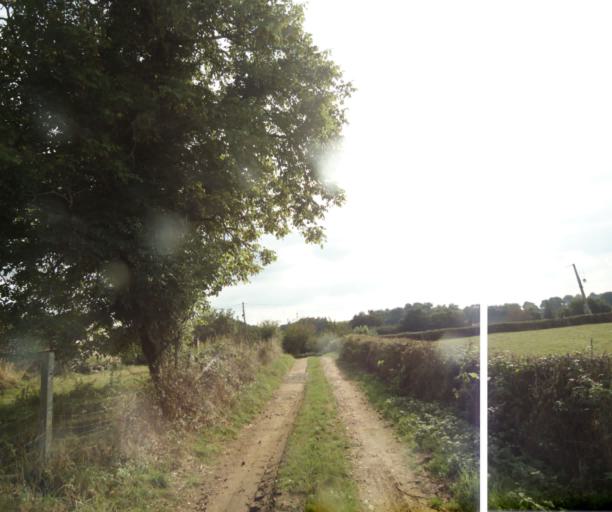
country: FR
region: Bourgogne
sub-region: Departement de Saone-et-Loire
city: Palinges
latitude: 46.5103
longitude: 4.2687
